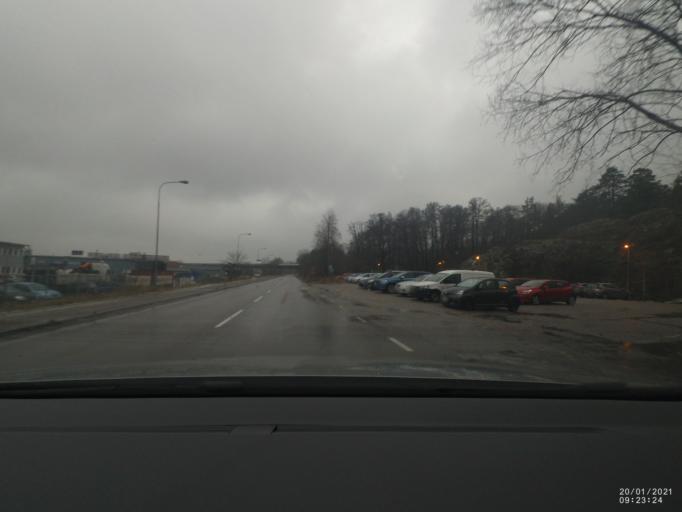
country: SE
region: Soedermanland
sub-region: Nykopings Kommun
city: Nykoping
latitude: 58.7583
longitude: 16.9892
